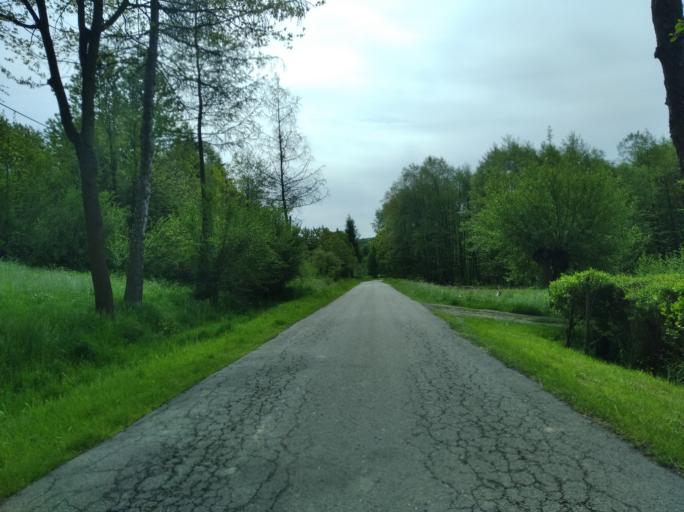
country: PL
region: Subcarpathian Voivodeship
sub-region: Powiat strzyzowski
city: Strzyzow
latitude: 49.9292
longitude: 21.7407
